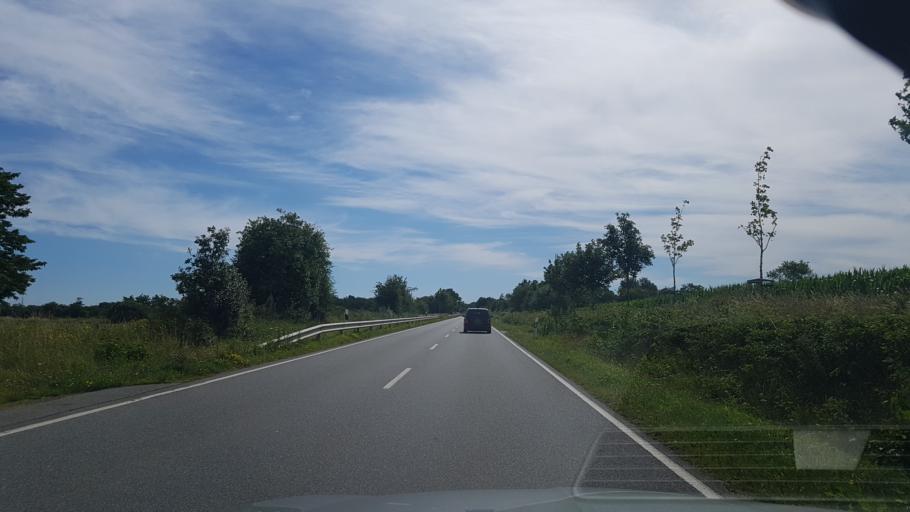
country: DE
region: Schleswig-Holstein
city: Wallsbull
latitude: 54.7976
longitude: 9.2832
